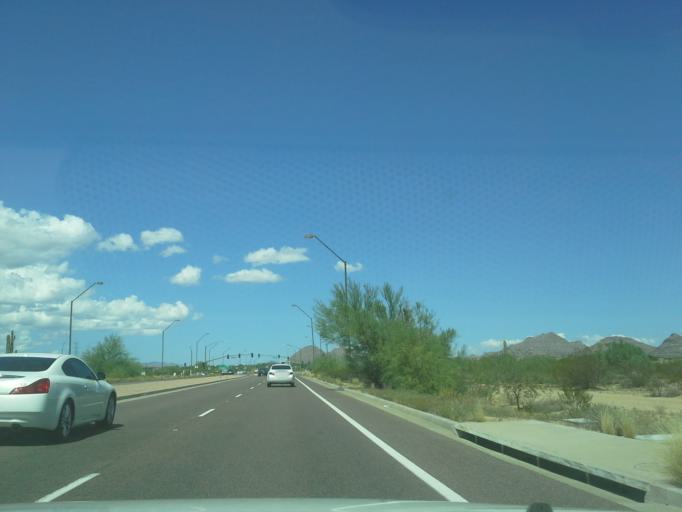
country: US
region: Arizona
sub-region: Maricopa County
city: Paradise Valley
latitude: 33.6599
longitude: -111.9072
